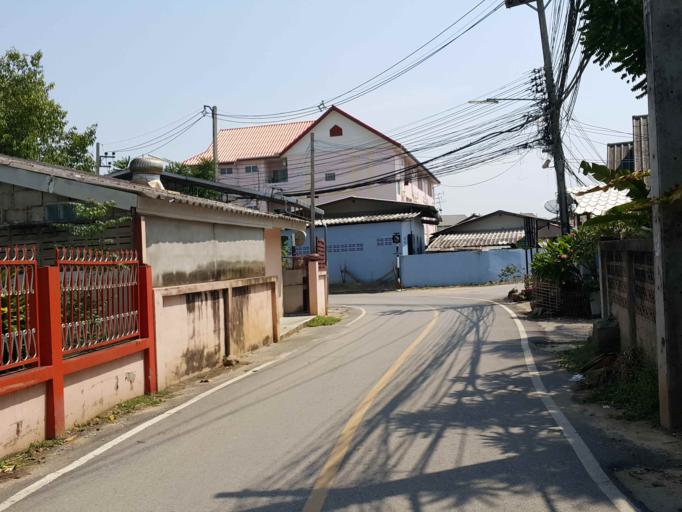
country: TH
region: Chiang Mai
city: Chiang Mai
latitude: 18.7505
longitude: 98.9561
